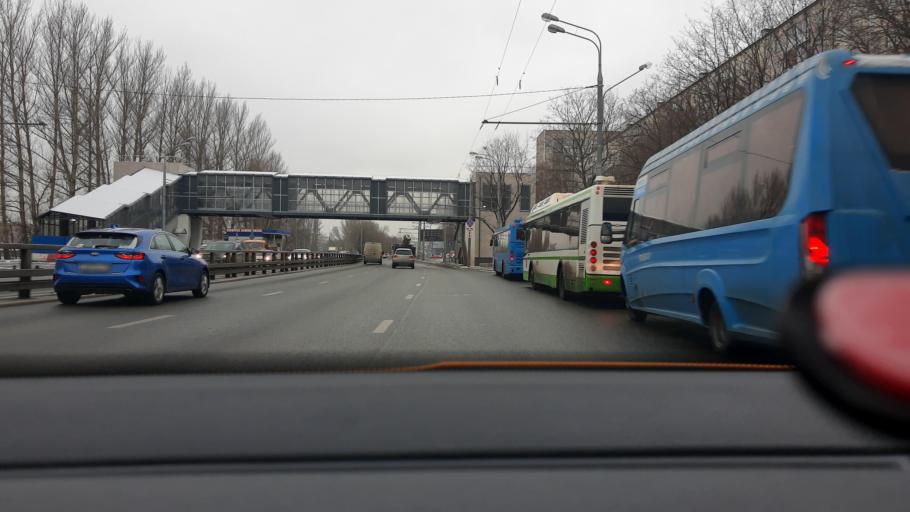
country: RU
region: Moscow
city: Likhobory
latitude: 55.8417
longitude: 37.5550
